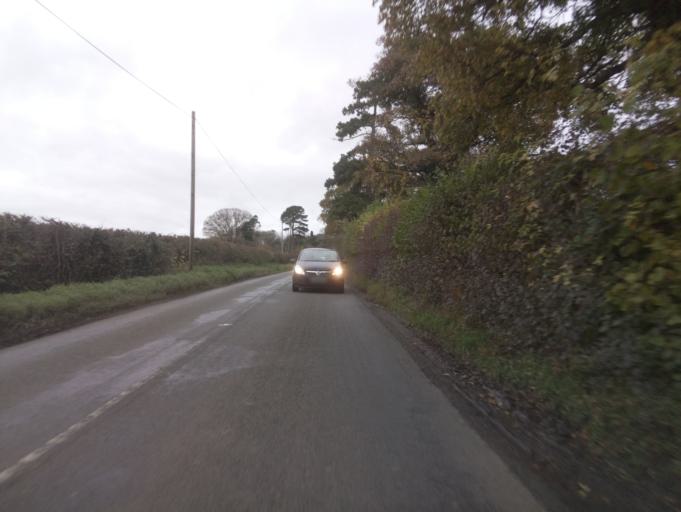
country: GB
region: England
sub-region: Somerset
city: Yeovil
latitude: 50.9947
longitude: -2.5802
